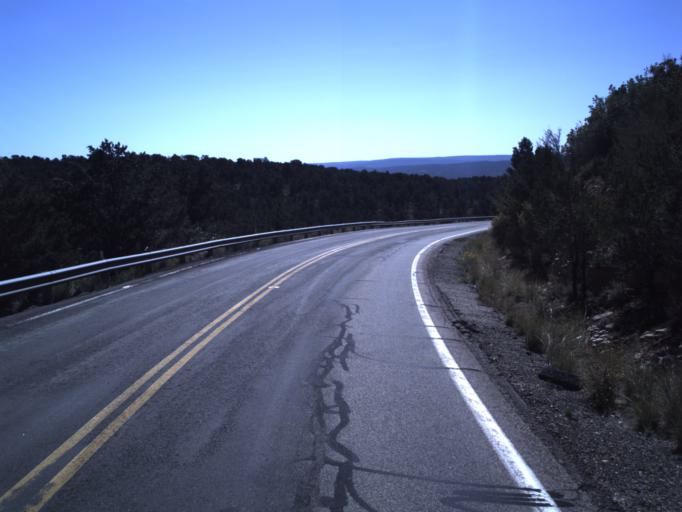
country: US
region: Utah
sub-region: Grand County
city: Moab
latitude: 38.3227
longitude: -109.2254
